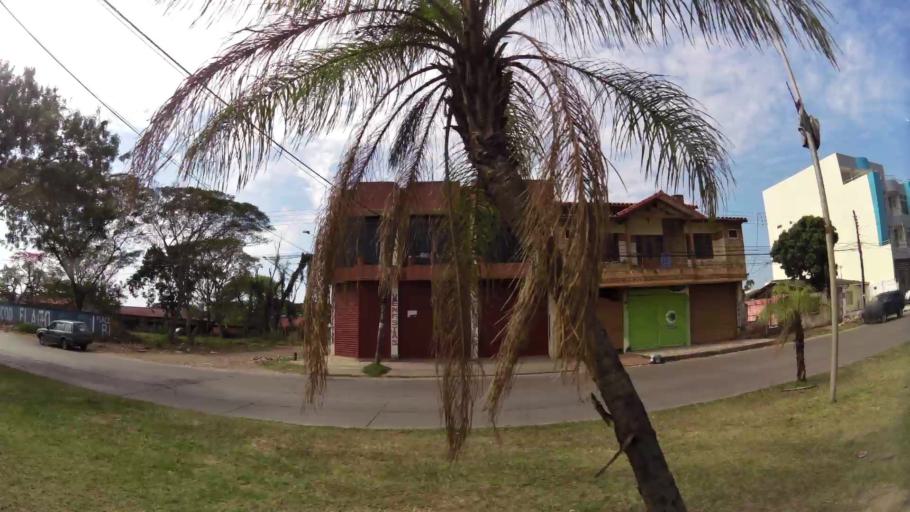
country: BO
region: Santa Cruz
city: Santa Cruz de la Sierra
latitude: -17.7496
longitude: -63.1539
